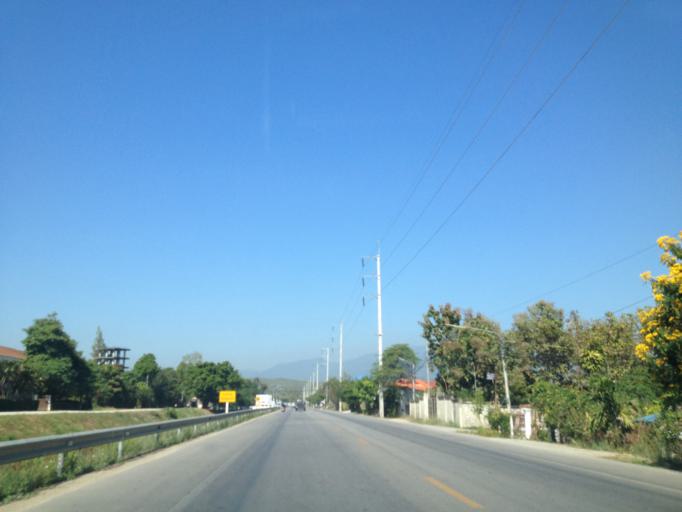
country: TH
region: Chiang Mai
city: Hang Dong
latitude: 18.6838
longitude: 98.8979
